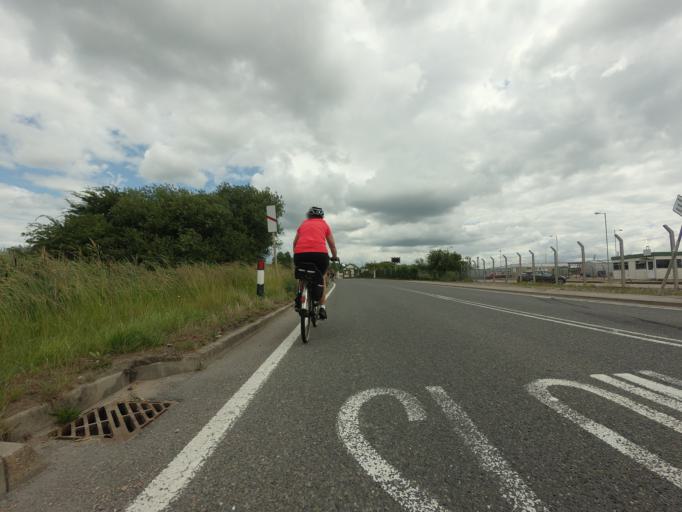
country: GB
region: England
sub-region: Medway
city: Allhallows
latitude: 51.4461
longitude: 0.6790
